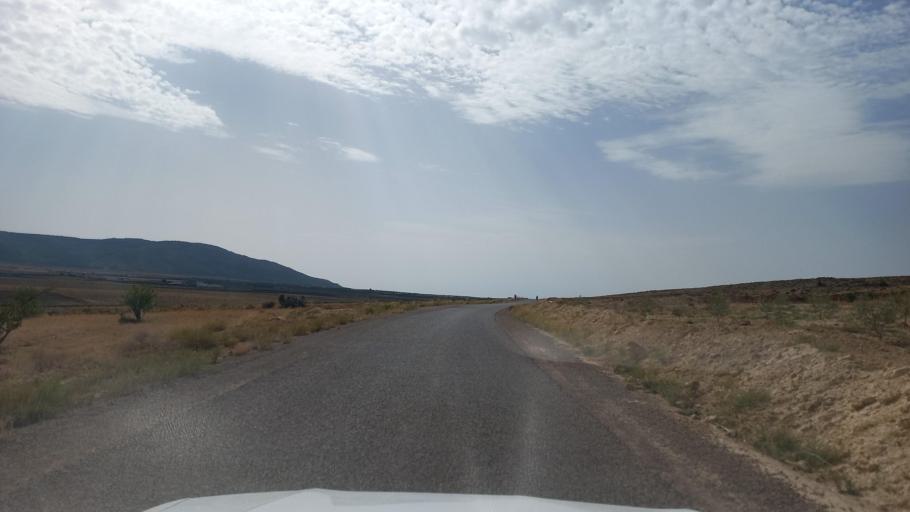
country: TN
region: Al Qasrayn
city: Kasserine
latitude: 35.3604
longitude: 8.8404
